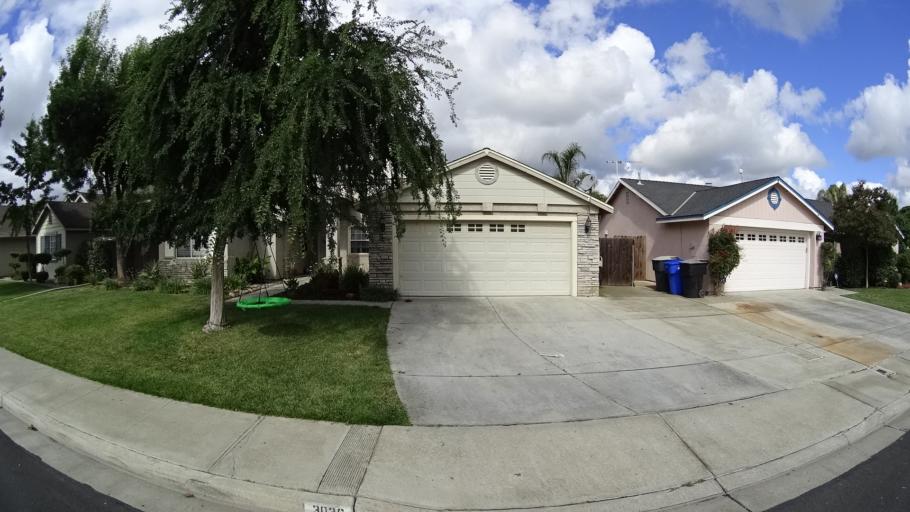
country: US
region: California
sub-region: Kings County
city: Lucerne
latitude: 36.3654
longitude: -119.6501
